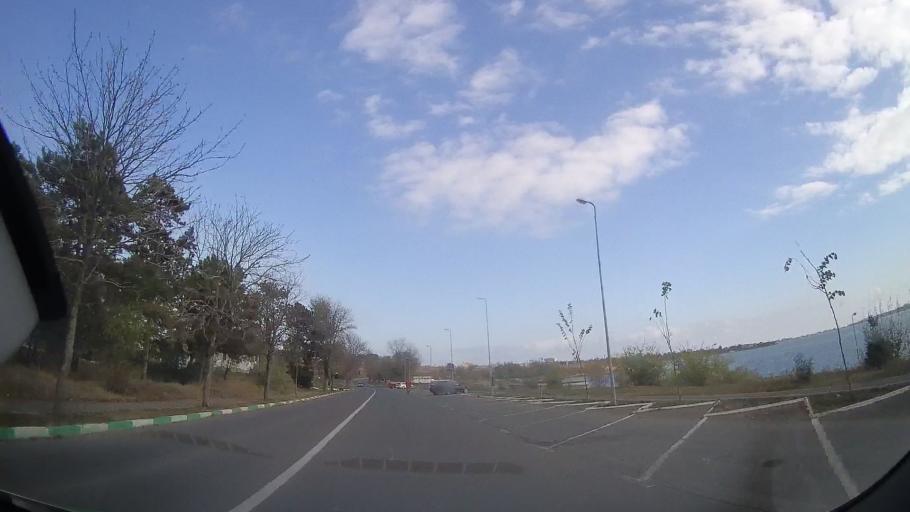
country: RO
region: Constanta
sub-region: Oras Techirghiol
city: Techirghiol
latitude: 44.0559
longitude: 28.6063
